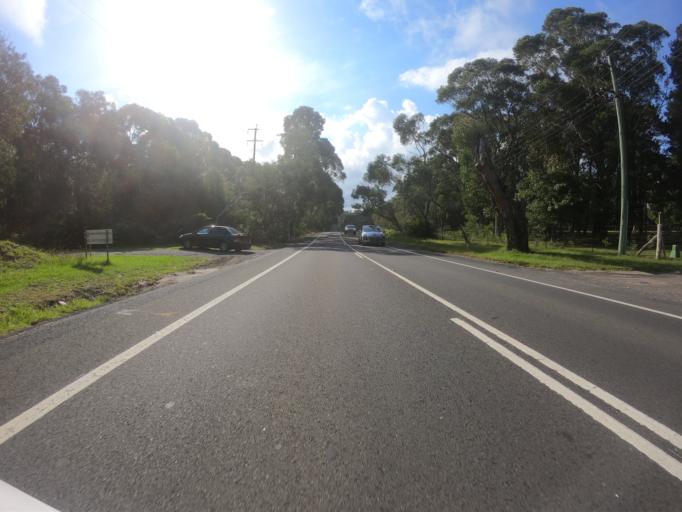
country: AU
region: New South Wales
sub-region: Wollongong
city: Helensburgh
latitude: -34.2162
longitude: 150.9777
